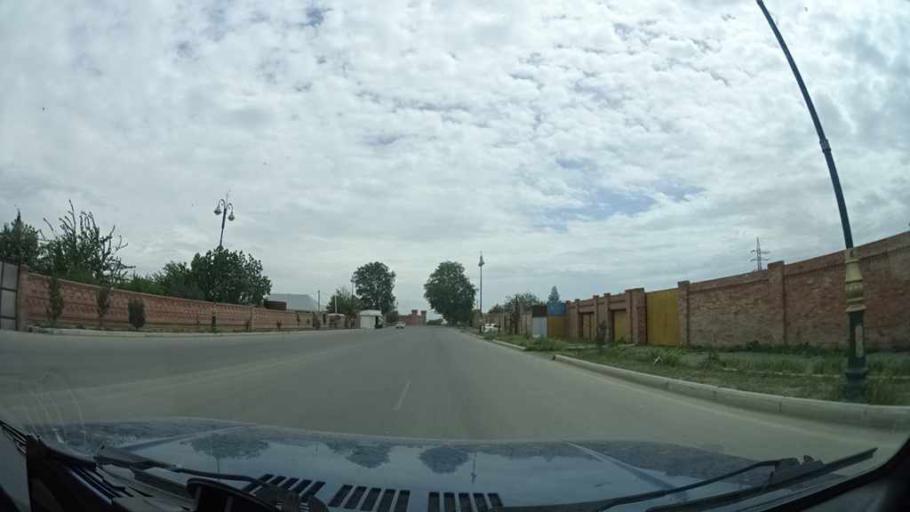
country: AZ
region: Samux
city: Samux
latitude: 40.7142
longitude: 46.4154
